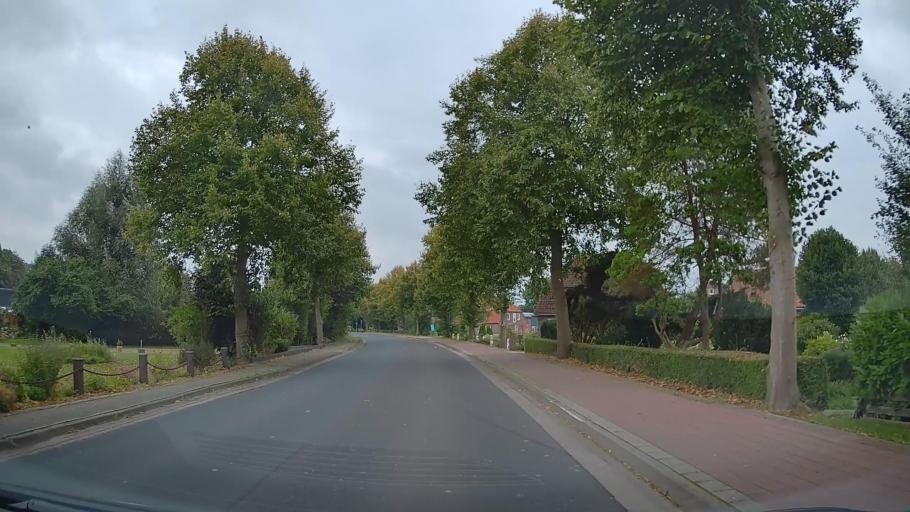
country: DE
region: Lower Saxony
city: Wischhafen
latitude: 53.7946
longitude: 9.3231
